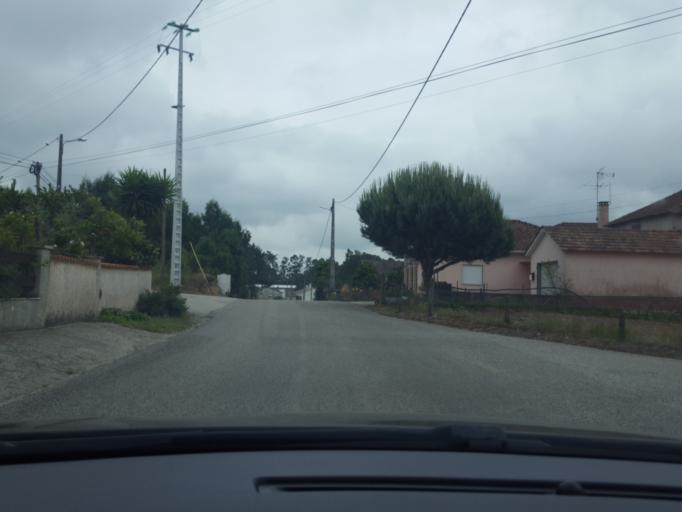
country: PT
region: Leiria
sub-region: Leiria
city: Caranguejeira
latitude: 39.7940
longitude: -8.7522
